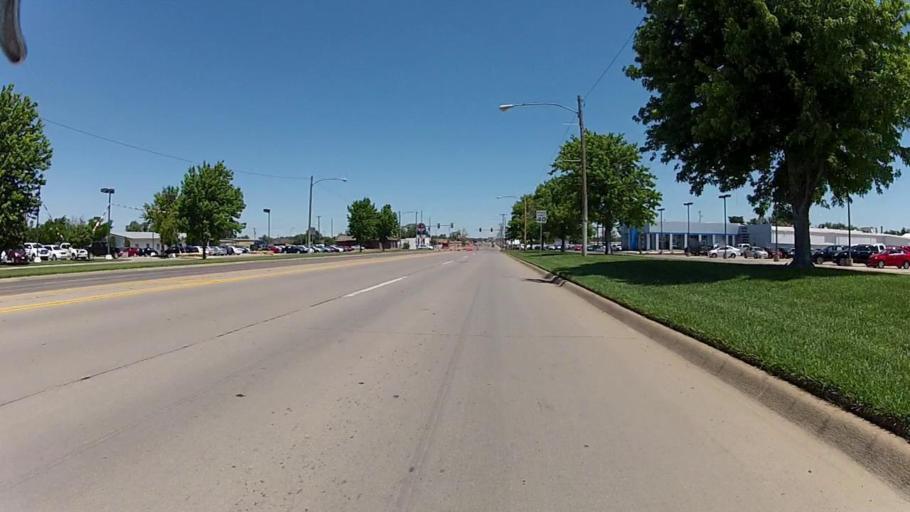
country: US
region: Kansas
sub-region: Ford County
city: Dodge City
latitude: 37.7353
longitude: -100.0194
